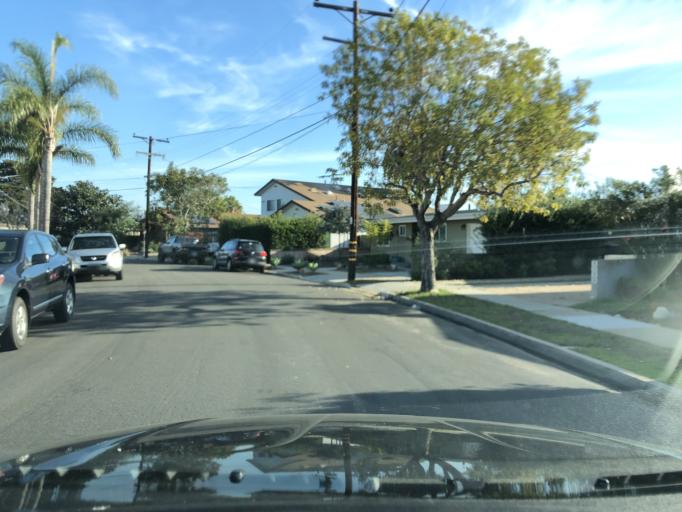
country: US
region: California
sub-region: San Diego County
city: La Jolla
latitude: 32.8290
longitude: -117.1958
